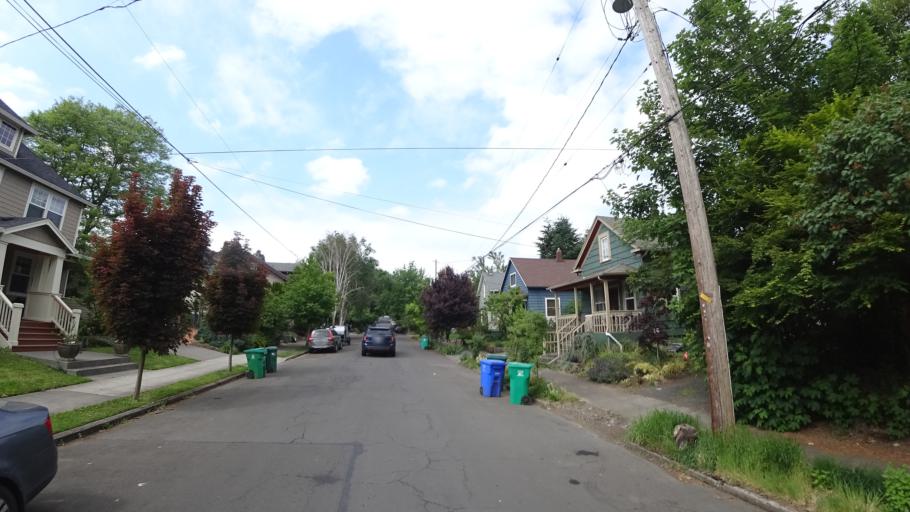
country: US
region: Oregon
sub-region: Multnomah County
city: Portland
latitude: 45.5515
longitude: -122.6528
